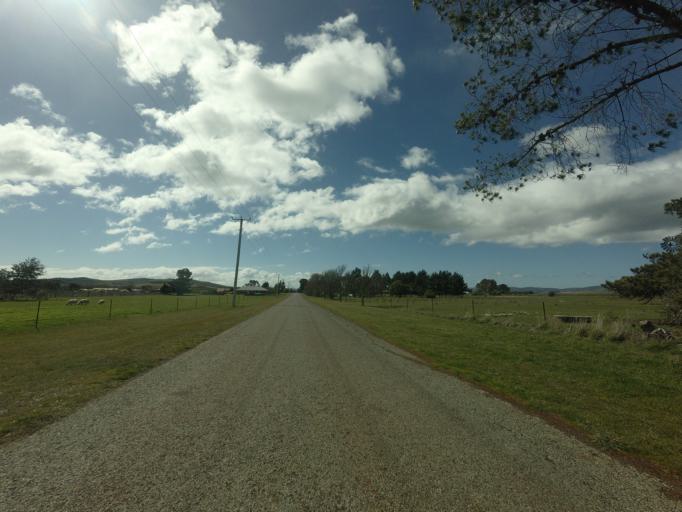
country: AU
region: Tasmania
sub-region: Northern Midlands
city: Evandale
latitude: -42.1444
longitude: 147.4198
